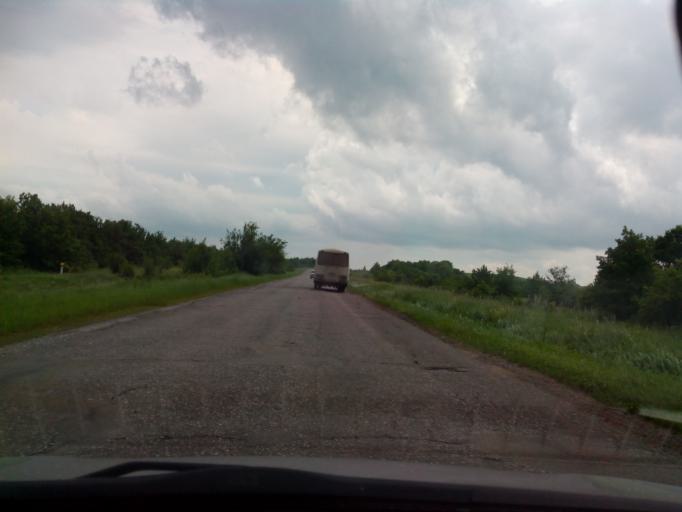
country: RU
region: Volgograd
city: Mikhaylovka
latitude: 49.9655
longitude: 43.0364
